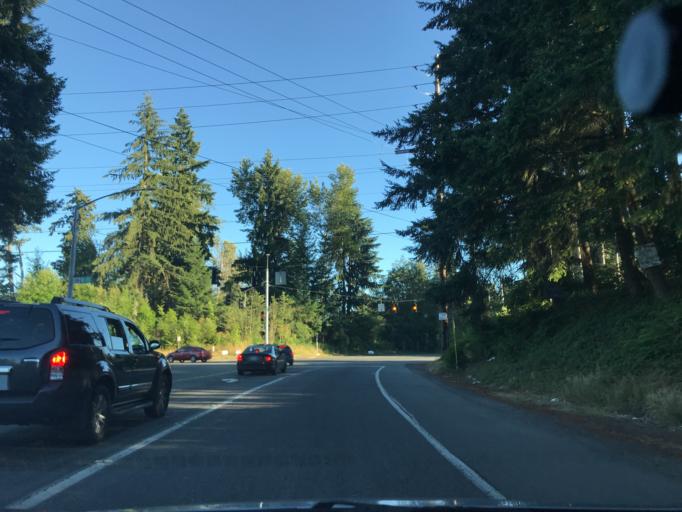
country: US
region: Washington
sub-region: King County
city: Pacific
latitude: 47.2511
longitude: -122.1871
